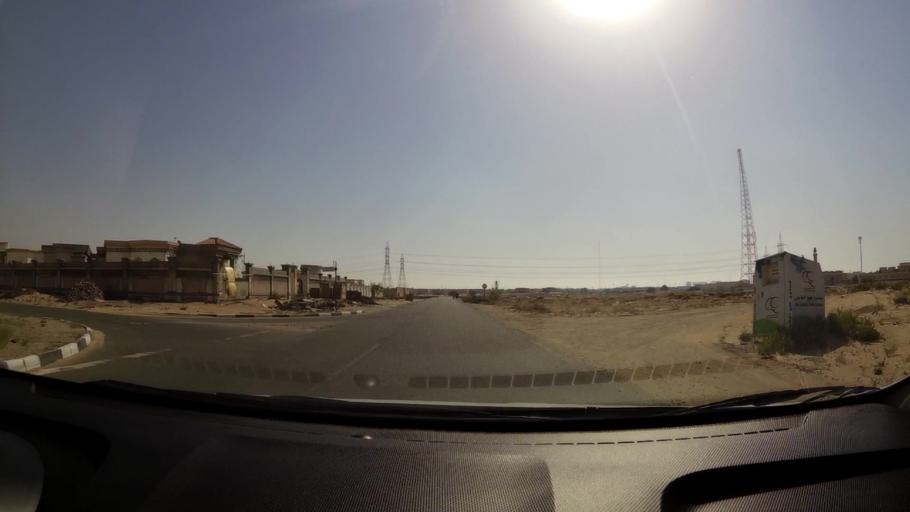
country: AE
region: Umm al Qaywayn
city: Umm al Qaywayn
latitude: 25.4860
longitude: 55.5831
